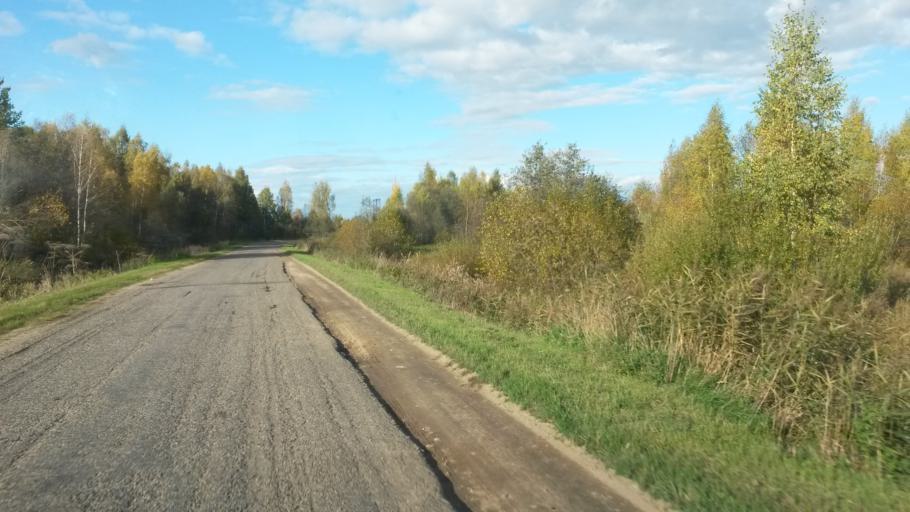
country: RU
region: Jaroslavl
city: Tunoshna
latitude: 57.5265
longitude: 40.0110
